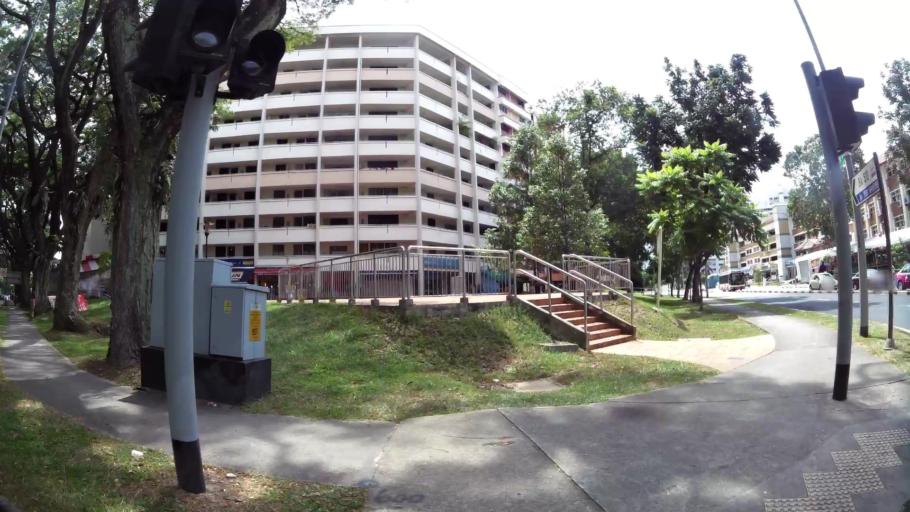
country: MY
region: Johor
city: Johor Bahru
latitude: 1.3508
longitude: 103.7193
